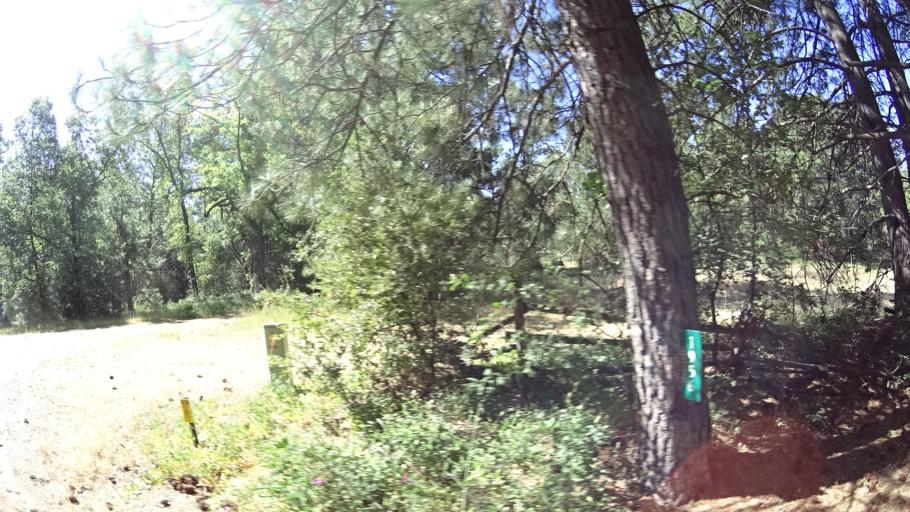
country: US
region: California
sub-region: Amador County
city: Pioneer
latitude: 38.3976
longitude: -120.4926
